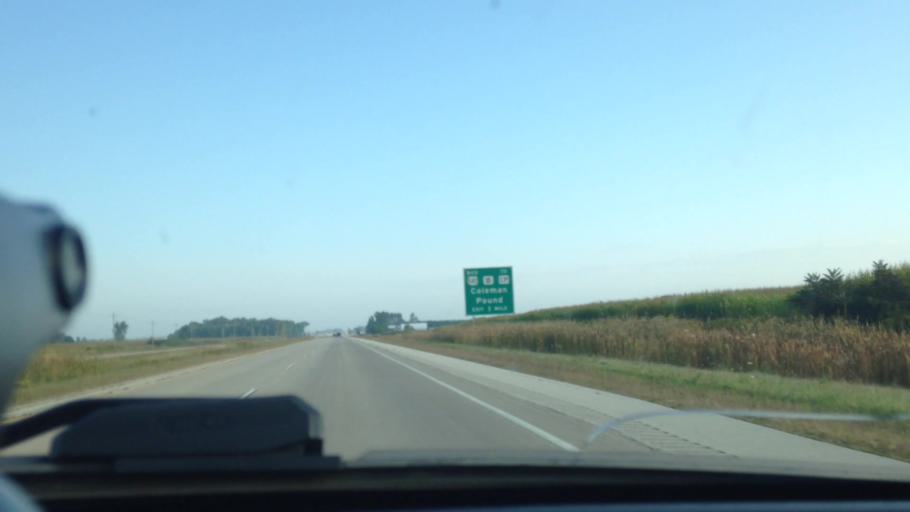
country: US
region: Wisconsin
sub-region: Oconto County
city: Oconto Falls
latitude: 45.0398
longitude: -88.0444
